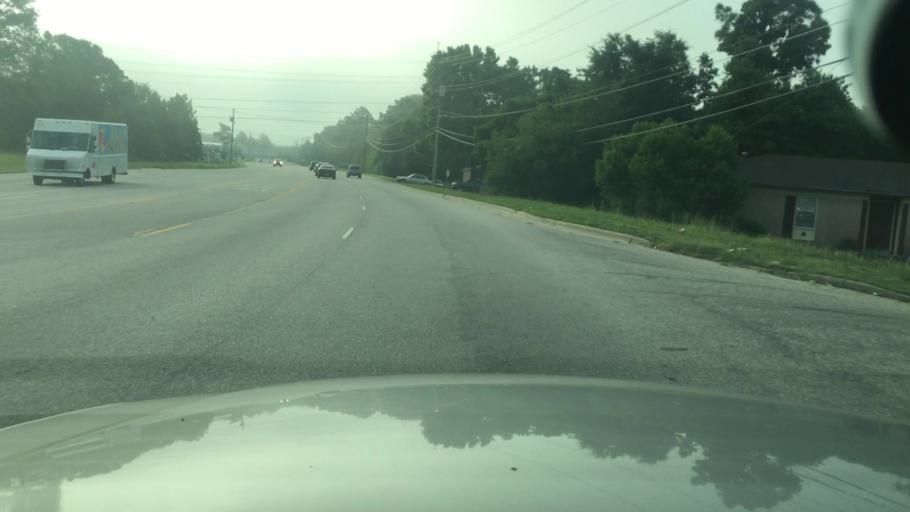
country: US
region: North Carolina
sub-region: Cumberland County
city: Hope Mills
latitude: 35.0026
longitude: -78.9144
